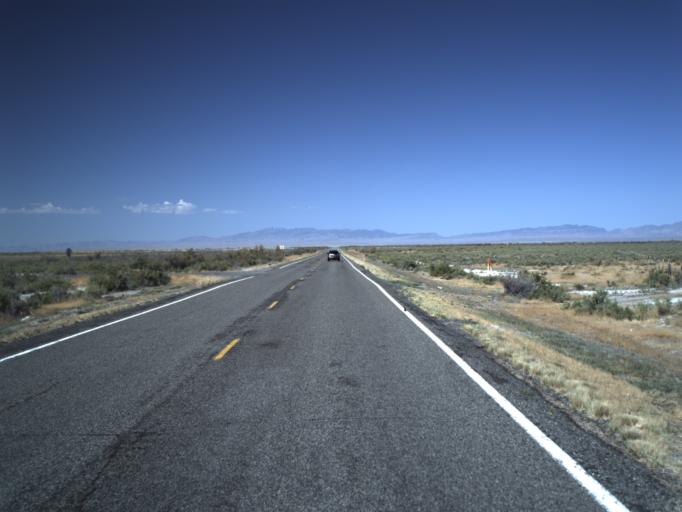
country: US
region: Utah
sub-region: Millard County
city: Delta
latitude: 39.3127
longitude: -112.7639
